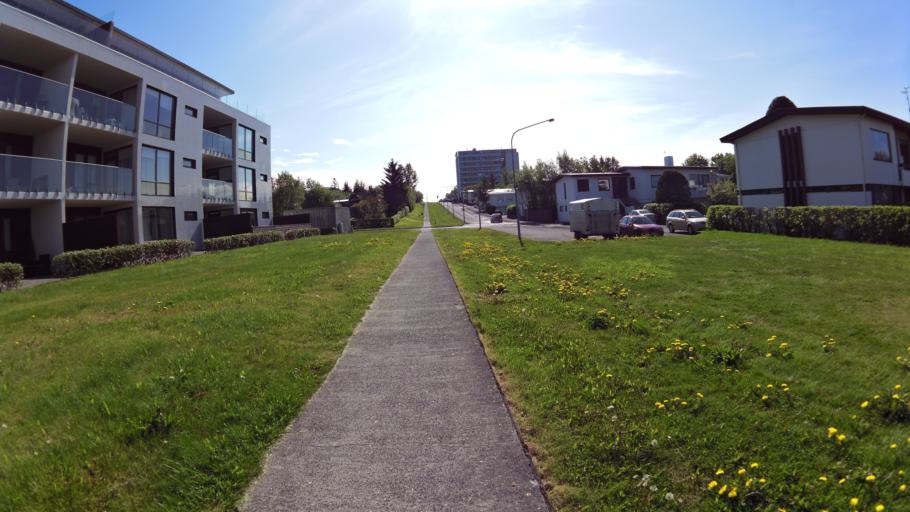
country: IS
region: Capital Region
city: Reykjavik
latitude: 64.1258
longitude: -21.8872
